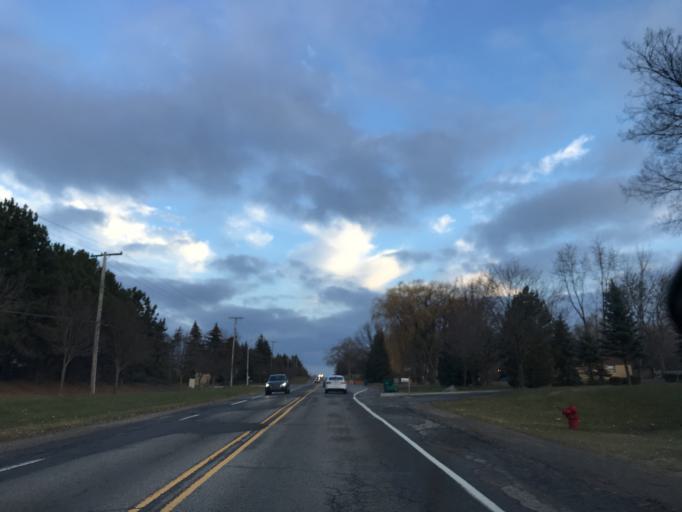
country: US
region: Michigan
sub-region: Oakland County
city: Novi
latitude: 42.4672
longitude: -83.4945
